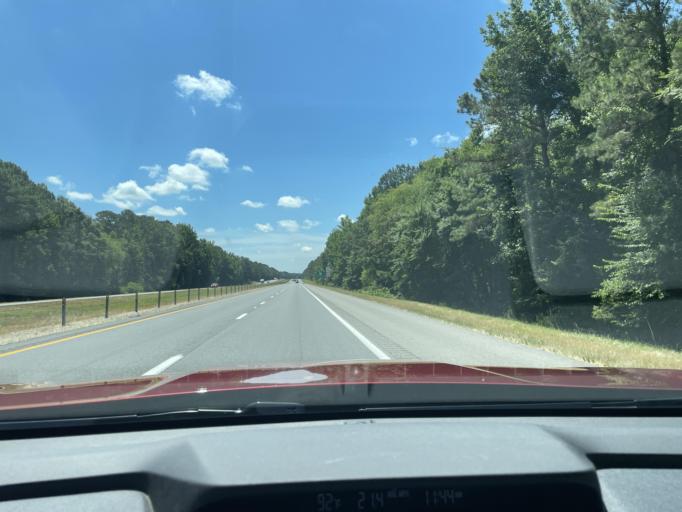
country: US
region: Arkansas
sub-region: Jefferson County
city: White Hall
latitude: 34.3023
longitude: -92.1343
